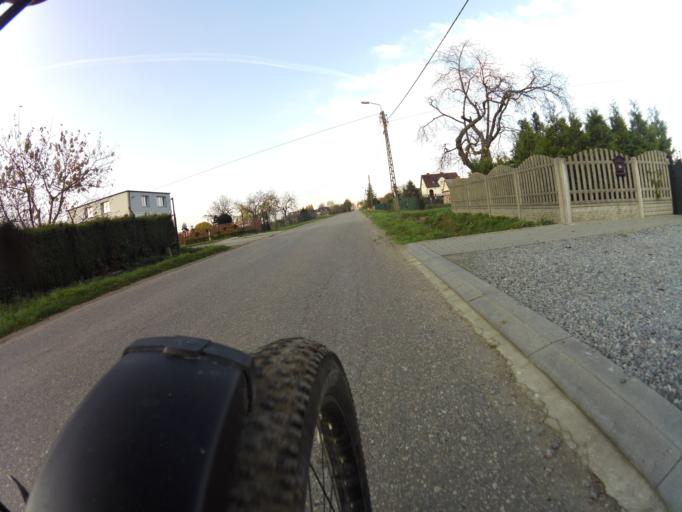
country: PL
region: Pomeranian Voivodeship
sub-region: Powiat pucki
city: Krokowa
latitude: 54.7579
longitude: 18.1838
